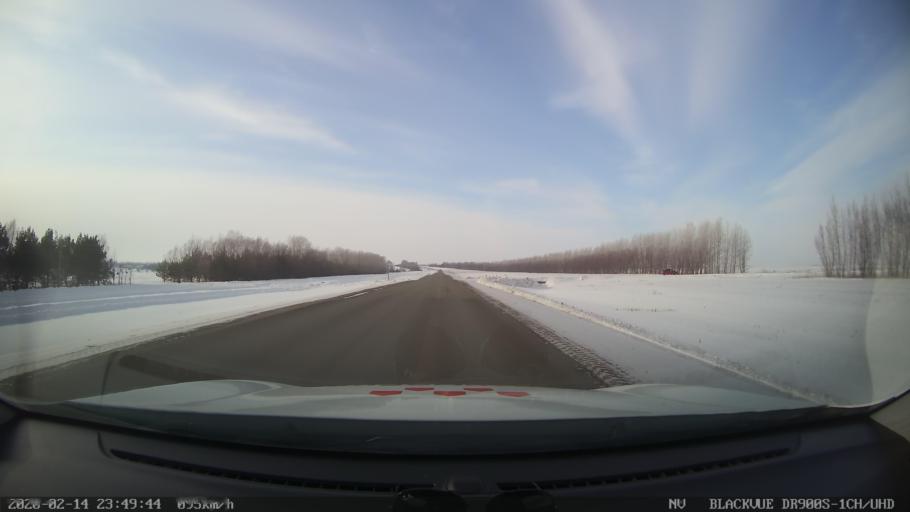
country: RU
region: Tatarstan
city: Kuybyshevskiy Zaton
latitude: 55.2556
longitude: 49.1747
